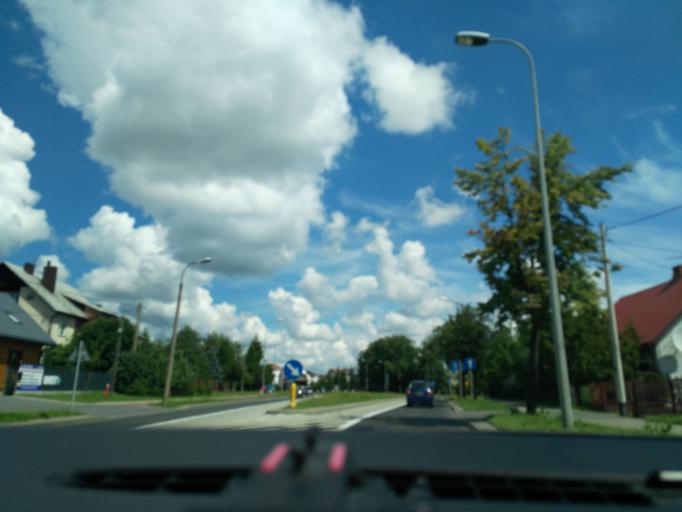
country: PL
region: Podlasie
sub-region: Powiat bielski
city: Bielsk Podlaski
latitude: 52.7772
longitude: 23.1873
